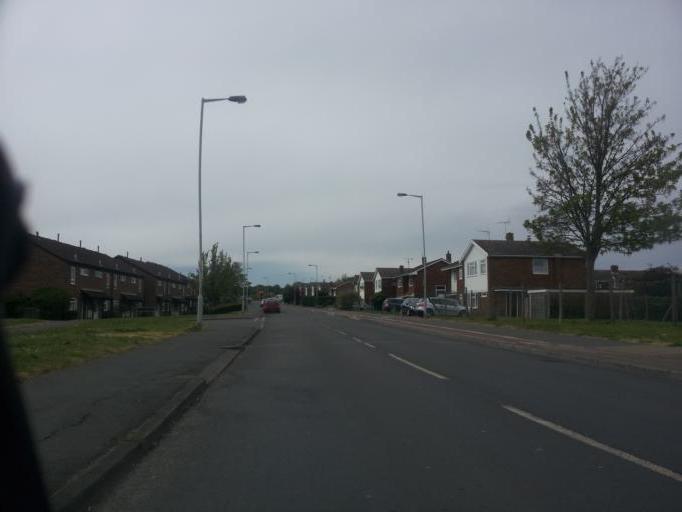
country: GB
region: England
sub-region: Kent
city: Faversham
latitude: 51.3210
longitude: 0.8789
